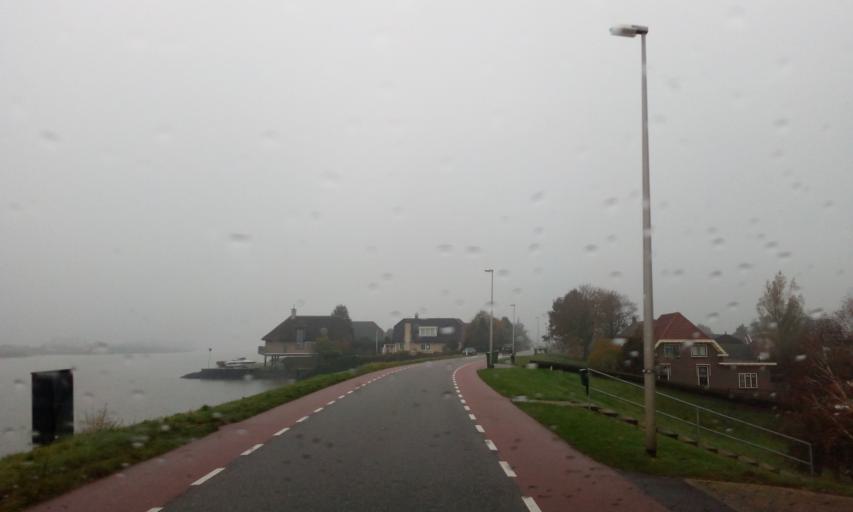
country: NL
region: South Holland
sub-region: Molenwaard
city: Nieuw-Lekkerland
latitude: 51.8986
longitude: 4.7169
